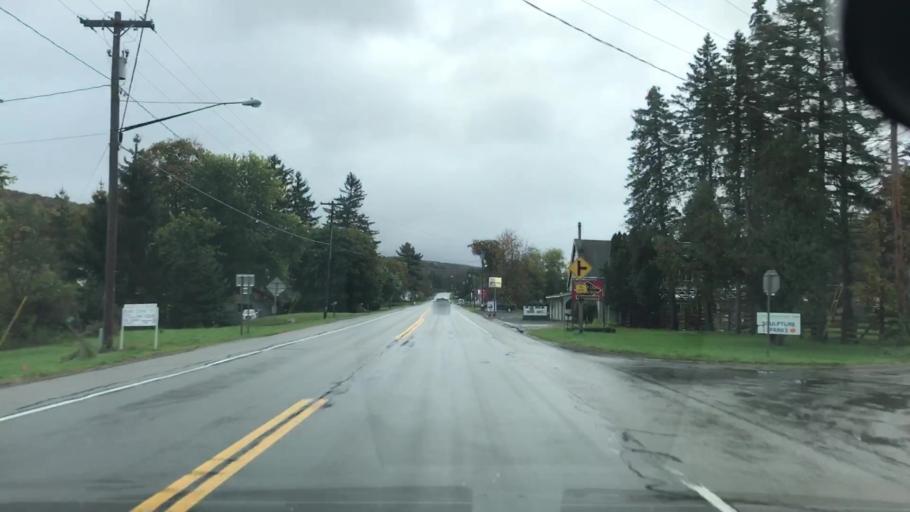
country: US
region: New York
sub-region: Erie County
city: Springville
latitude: 42.4033
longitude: -78.6855
